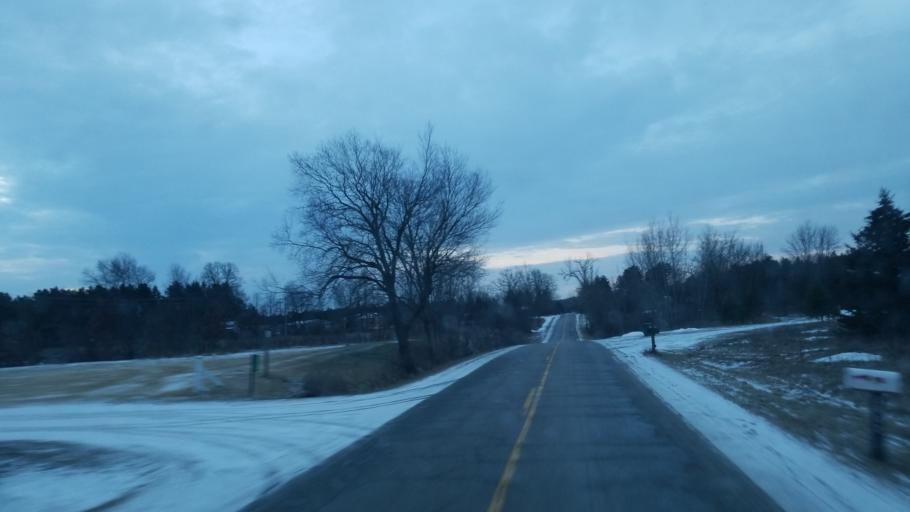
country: US
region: Michigan
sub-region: Osceola County
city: Reed City
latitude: 43.8344
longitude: -85.4242
